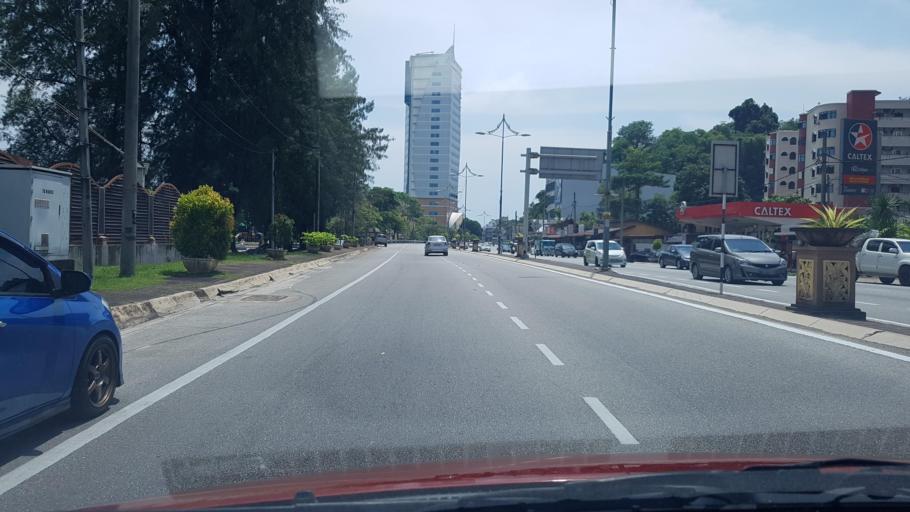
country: MY
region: Terengganu
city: Kuala Terengganu
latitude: 5.3259
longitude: 103.1325
